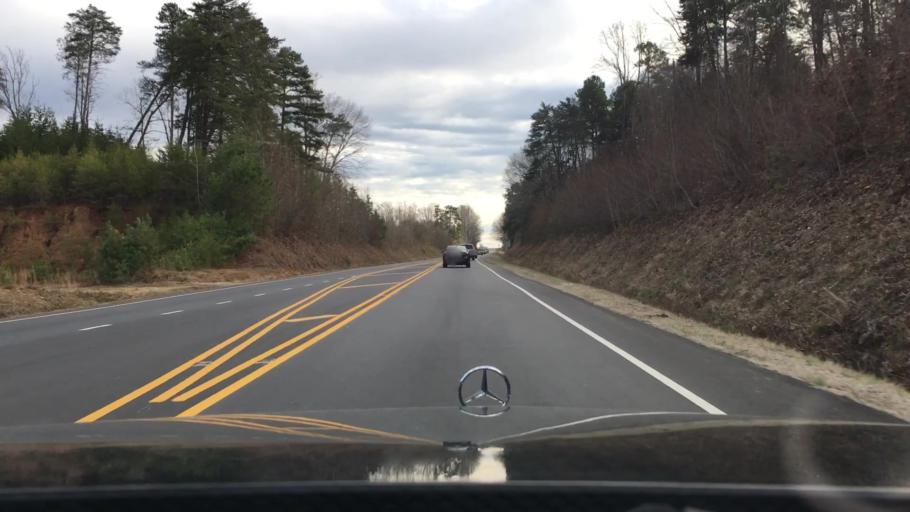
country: US
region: North Carolina
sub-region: Caswell County
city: Yanceyville
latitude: 36.4392
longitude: -79.3623
